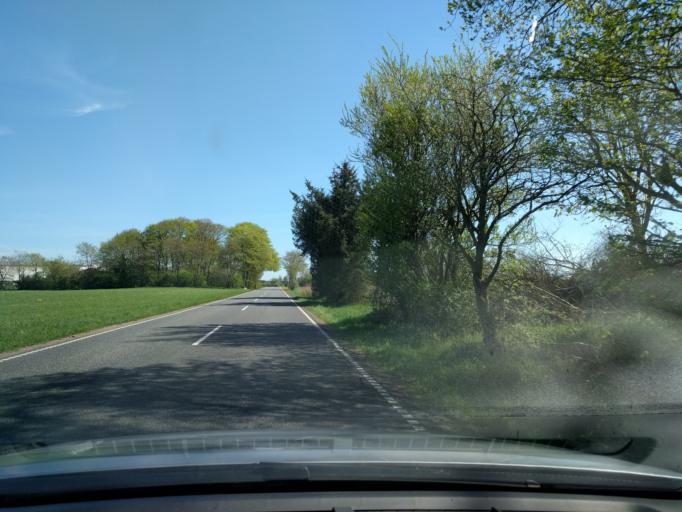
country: DK
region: South Denmark
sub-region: Billund Kommune
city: Grindsted
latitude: 55.6770
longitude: 8.9372
